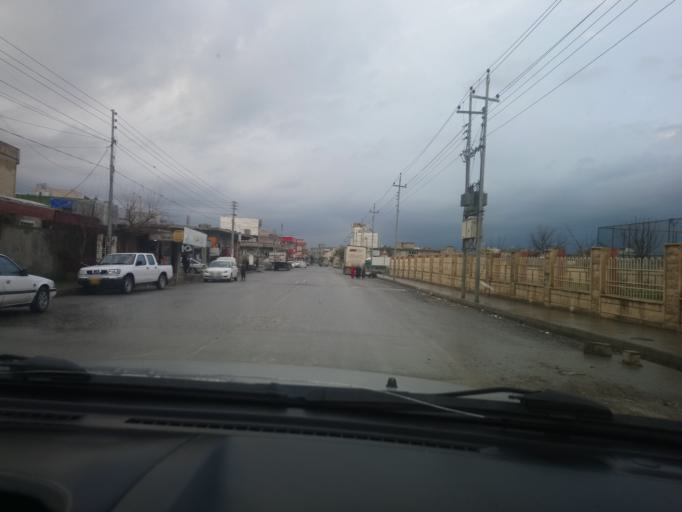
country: IQ
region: As Sulaymaniyah
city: Qeladize
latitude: 36.1818
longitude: 45.1365
